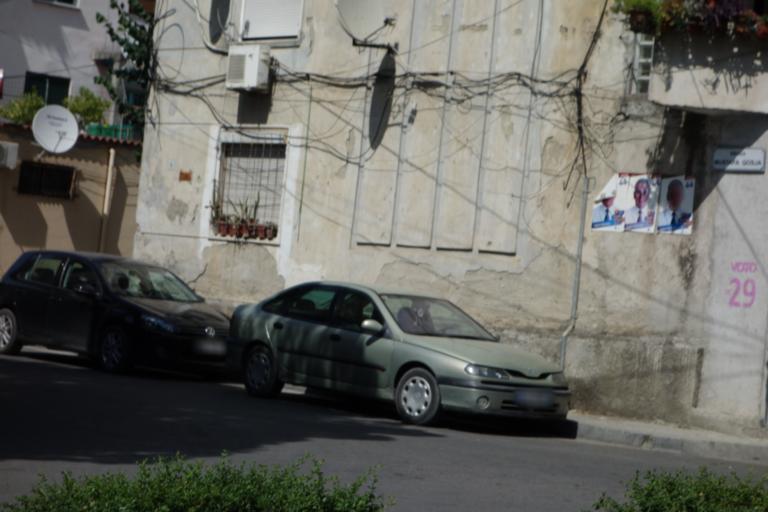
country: AL
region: Tirane
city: Tirana
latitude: 41.3203
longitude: 19.8061
